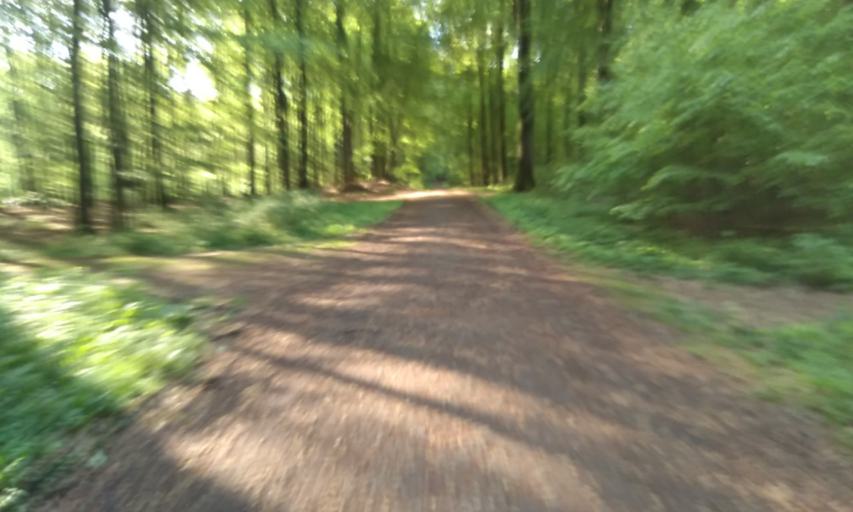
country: DE
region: Lower Saxony
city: Nottensdorf
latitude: 53.4750
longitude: 9.6396
